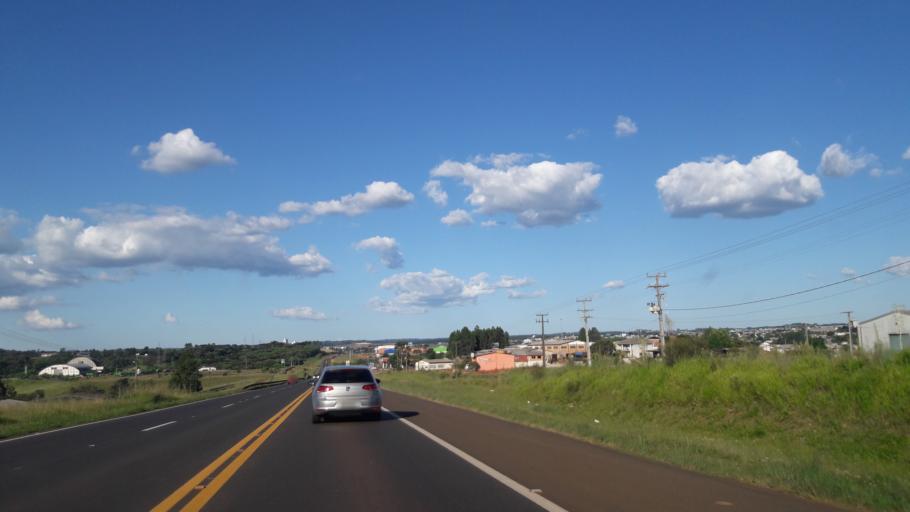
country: BR
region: Parana
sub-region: Guarapuava
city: Guarapuava
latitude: -25.3796
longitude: -51.5079
